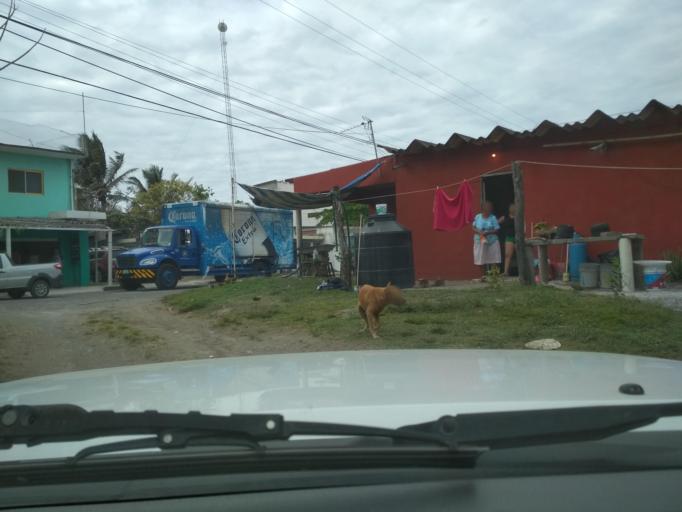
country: MX
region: Veracruz
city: Anton Lizardo
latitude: 19.0548
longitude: -95.9861
